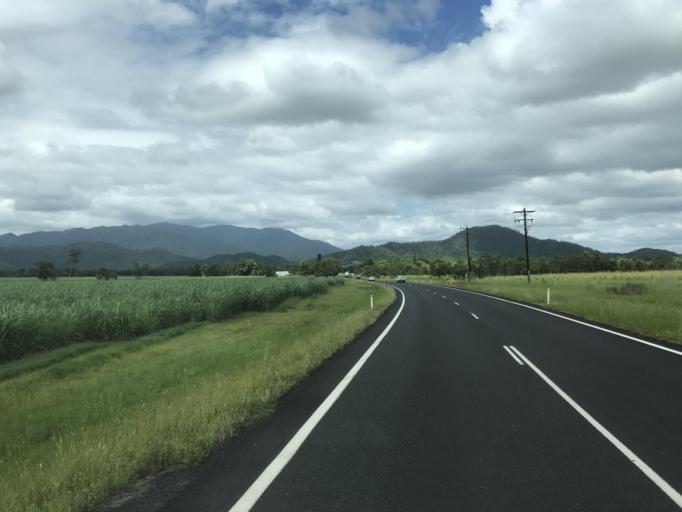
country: AU
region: Queensland
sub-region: Cassowary Coast
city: Innisfail
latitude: -17.8110
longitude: 146.0239
